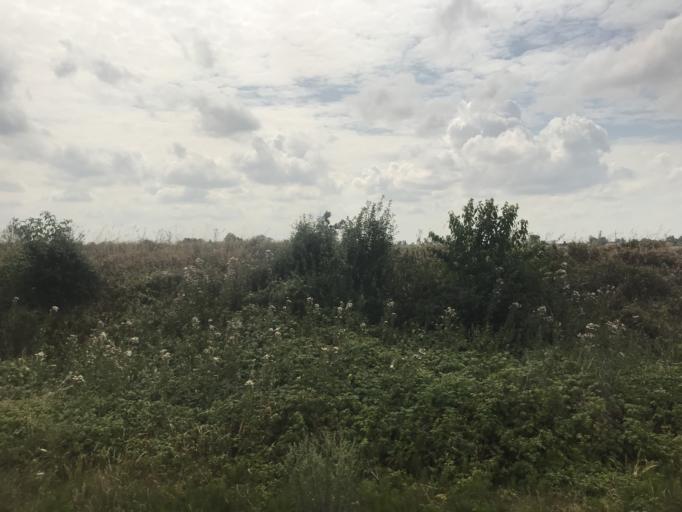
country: PL
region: Greater Poland Voivodeship
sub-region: Powiat gnieznienski
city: Gniezno
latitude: 52.5174
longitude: 17.5422
